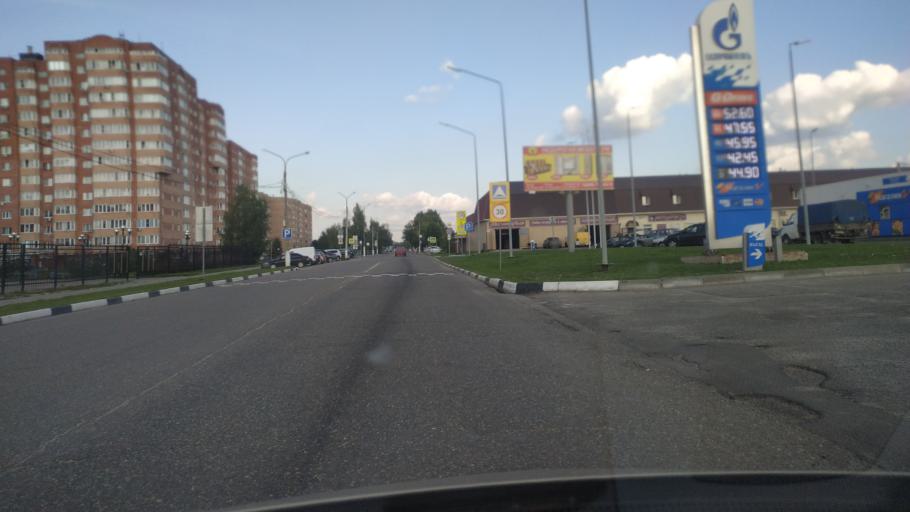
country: RU
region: Moskovskaya
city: Shatura
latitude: 55.5755
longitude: 39.5122
